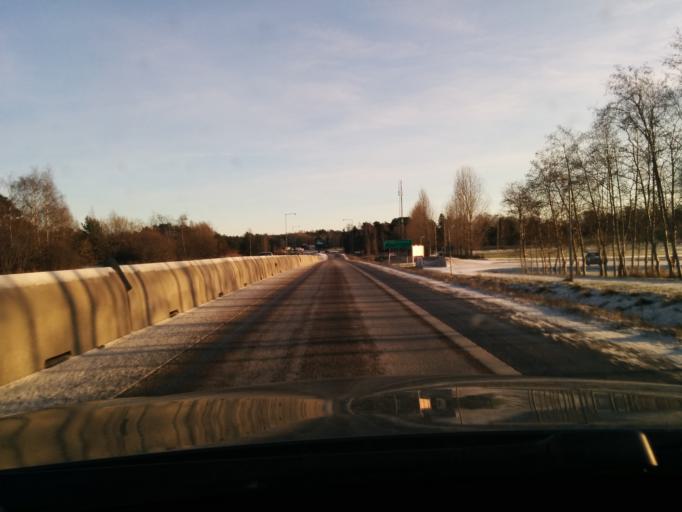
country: SE
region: Stockholm
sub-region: Upplands Vasby Kommun
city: Upplands Vaesby
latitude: 59.4721
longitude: 17.9022
